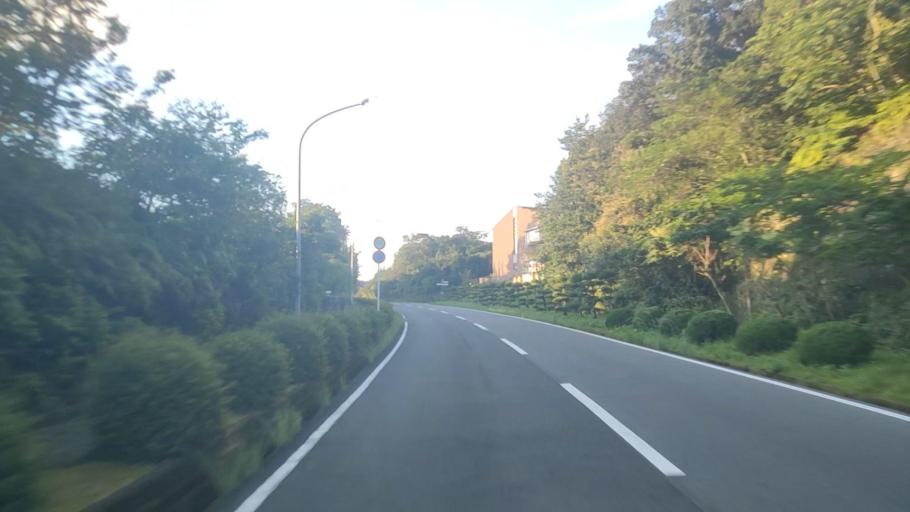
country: JP
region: Mie
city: Toba
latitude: 34.3186
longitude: 136.8166
